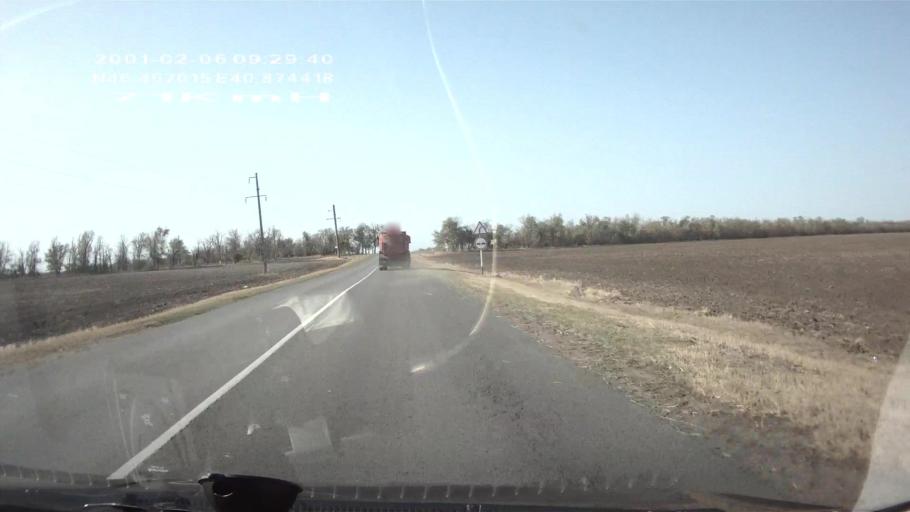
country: RU
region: Rostov
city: Tselina
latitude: 46.4667
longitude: 40.8741
